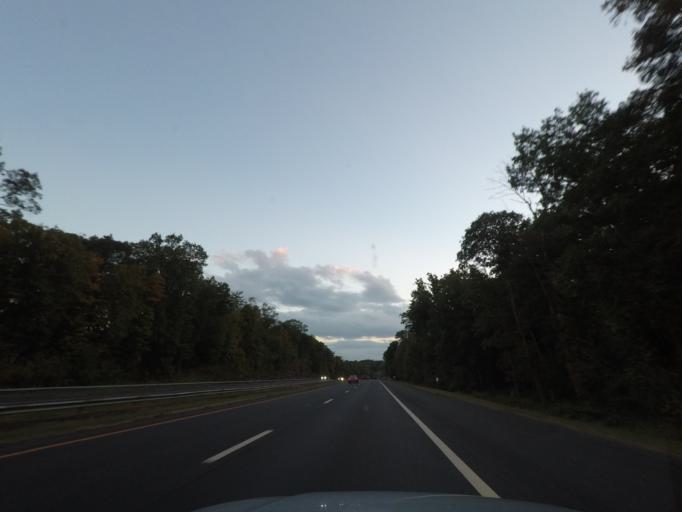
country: US
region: New York
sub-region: Ulster County
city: Hurley
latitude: 41.8949
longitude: -74.0465
